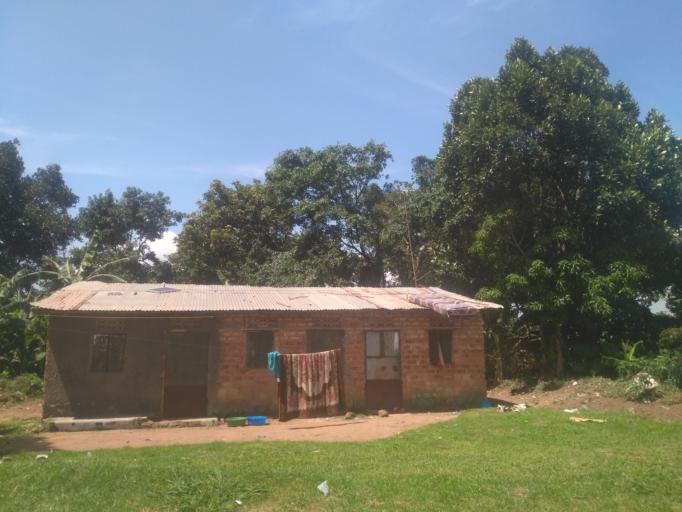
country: UG
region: Central Region
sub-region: Wakiso District
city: Entebbe
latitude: 0.0389
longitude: 32.4234
